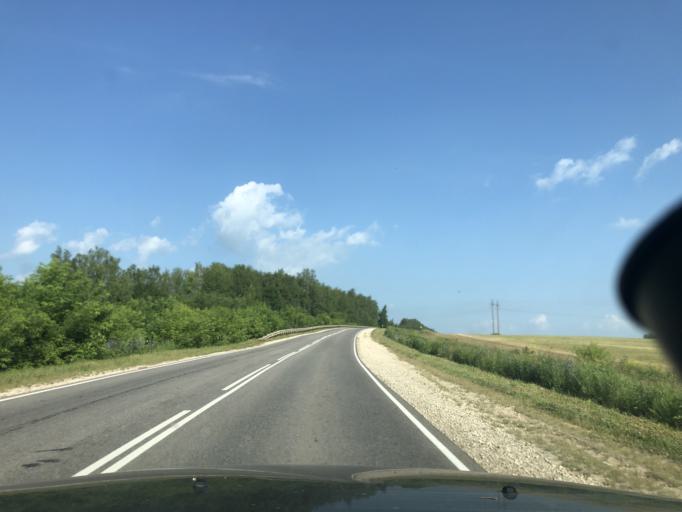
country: RU
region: Tula
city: Dubna
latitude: 54.1159
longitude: 37.0841
